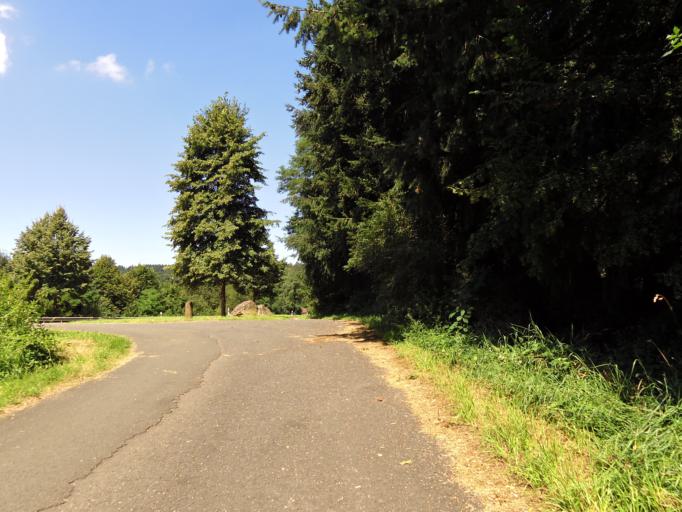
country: DE
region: Rheinland-Pfalz
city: Winnweiler
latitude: 49.5819
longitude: 7.8421
